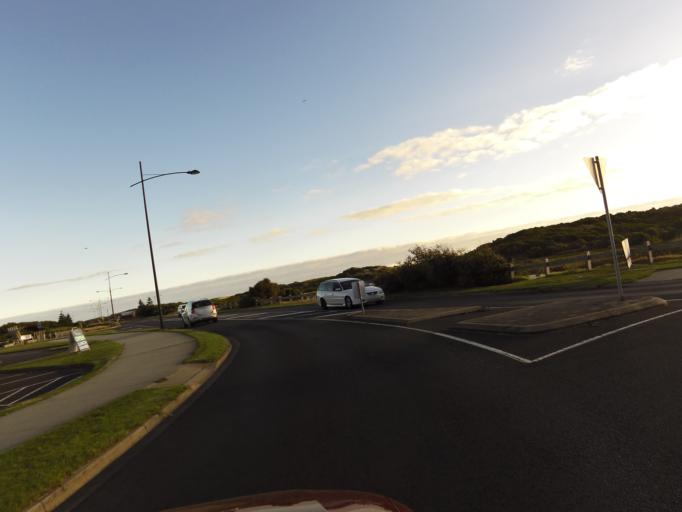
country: AU
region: Victoria
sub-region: Warrnambool
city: Warrnambool
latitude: -38.3967
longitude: 142.4721
